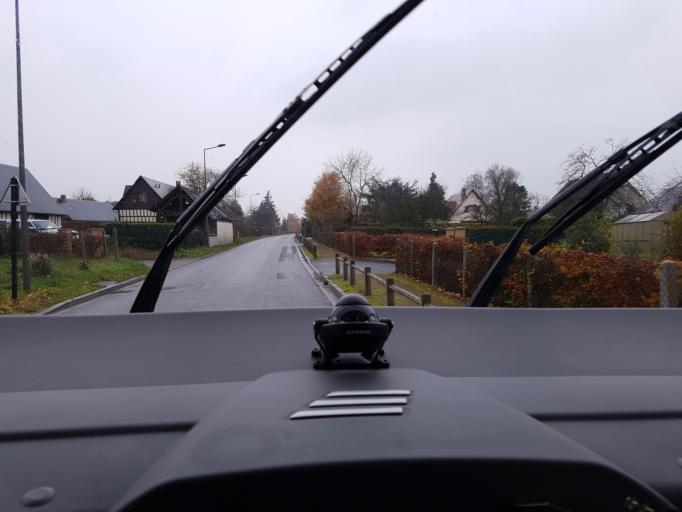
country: FR
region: Haute-Normandie
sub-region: Departement de la Seine-Maritime
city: Caudebec-en-Caux
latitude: 49.5048
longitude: 0.7067
